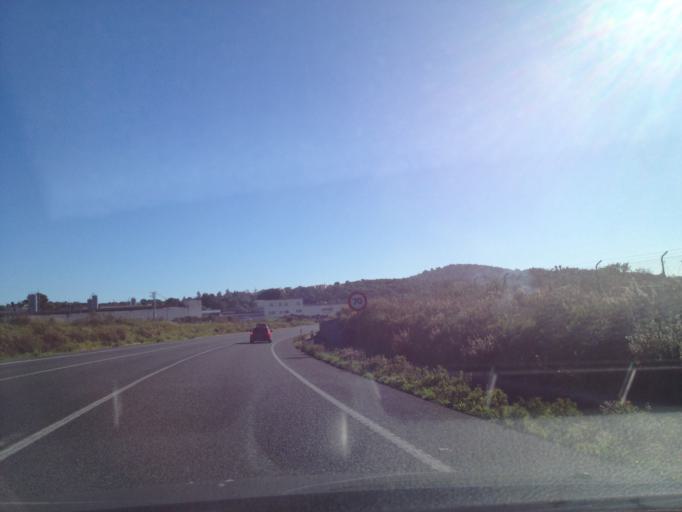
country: ES
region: Balearic Islands
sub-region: Illes Balears
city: Manacor
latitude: 39.5860
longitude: 3.2294
